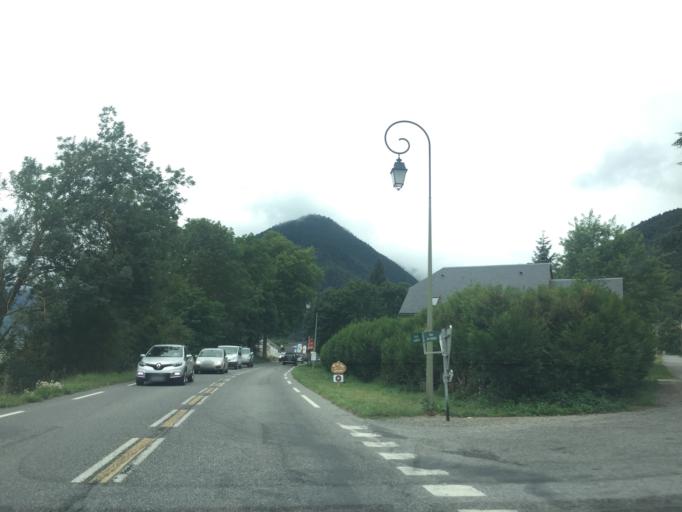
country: FR
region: Midi-Pyrenees
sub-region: Departement des Hautes-Pyrenees
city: Saint-Lary-Soulan
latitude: 42.8758
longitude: 0.3441
